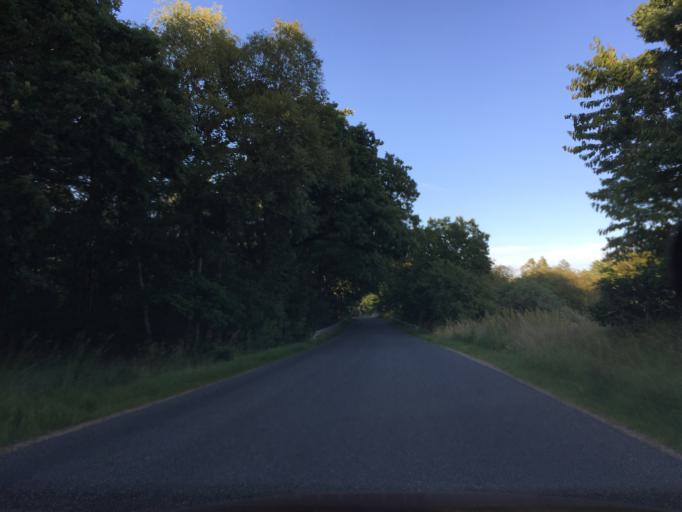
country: DK
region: Central Jutland
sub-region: Silkeborg Kommune
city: Svejbaek
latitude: 56.2398
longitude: 9.6678
